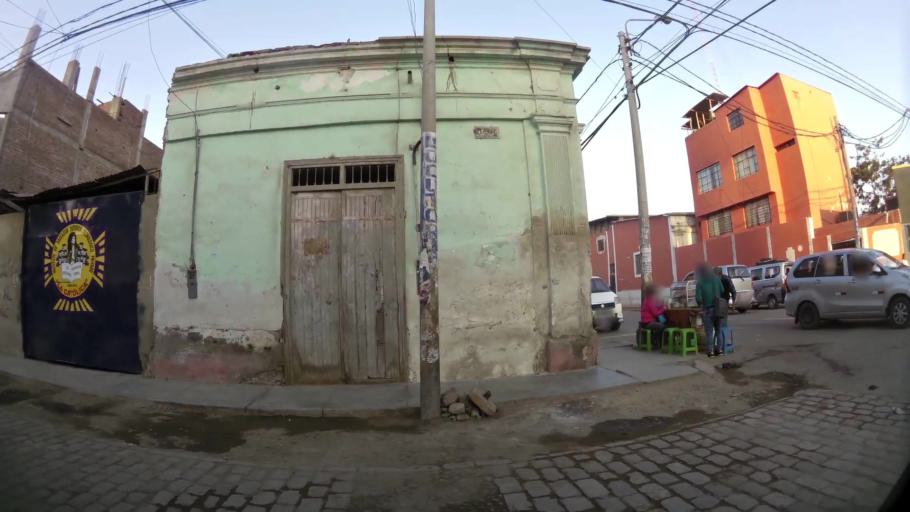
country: PE
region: Lambayeque
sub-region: Provincia de Chiclayo
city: Santa Rosa
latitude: -6.7694
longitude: -79.8352
